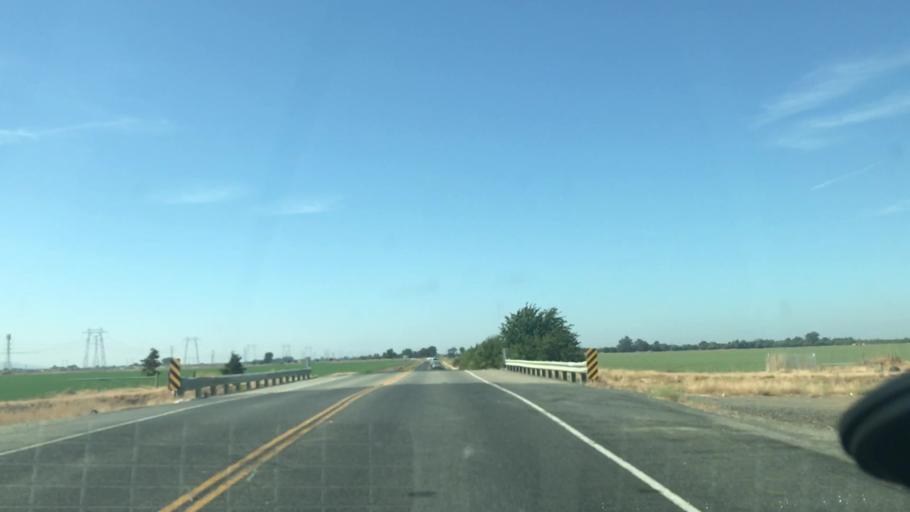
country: US
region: California
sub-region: Solano County
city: Vacaville
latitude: 38.3298
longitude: -121.9158
